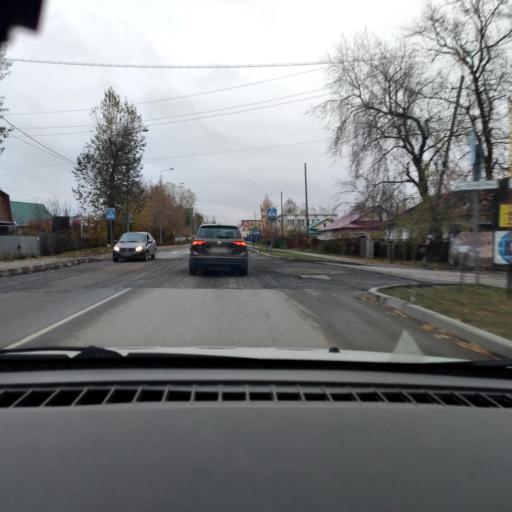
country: RU
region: Perm
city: Kondratovo
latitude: 57.9636
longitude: 56.1559
